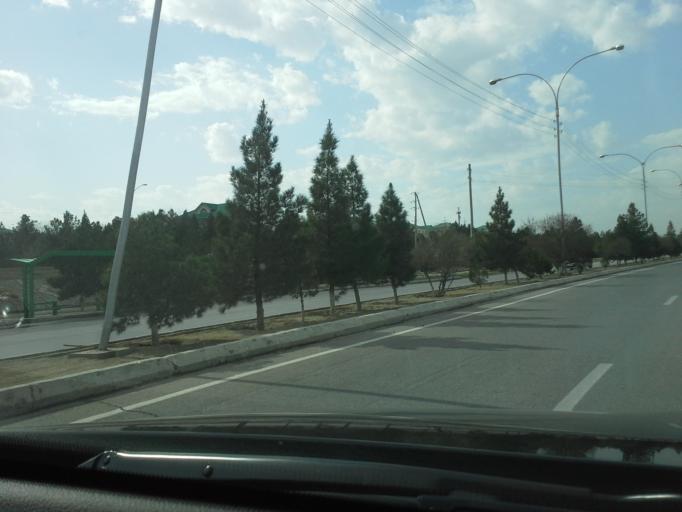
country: TM
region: Ahal
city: Ashgabat
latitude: 37.9591
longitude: 58.3186
